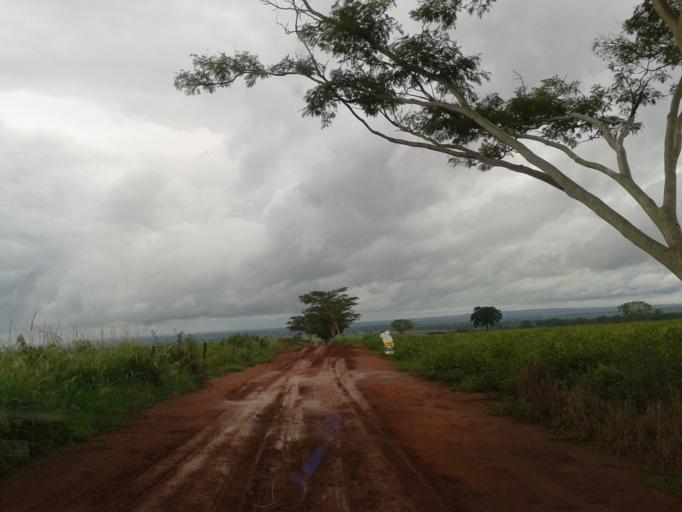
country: BR
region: Minas Gerais
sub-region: Santa Vitoria
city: Santa Vitoria
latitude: -18.7156
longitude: -49.9663
